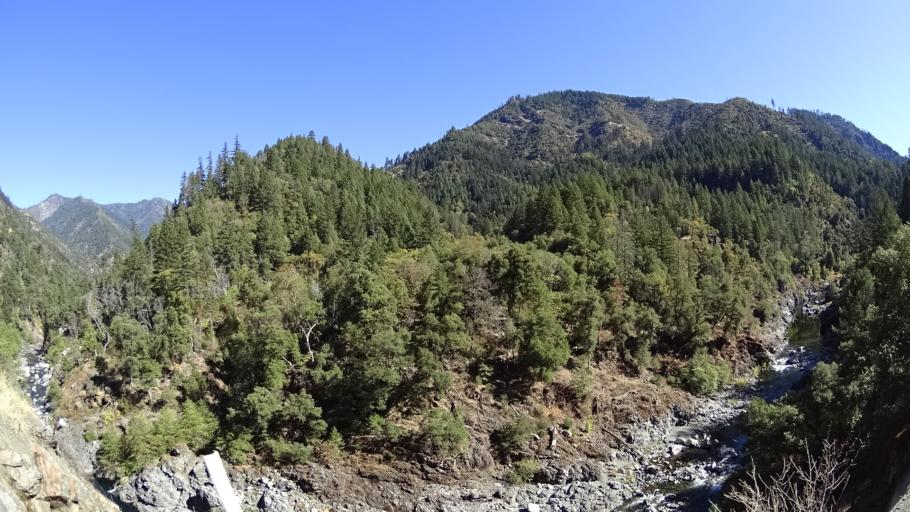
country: US
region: California
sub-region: Humboldt County
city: Willow Creek
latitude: 41.3178
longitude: -123.3814
